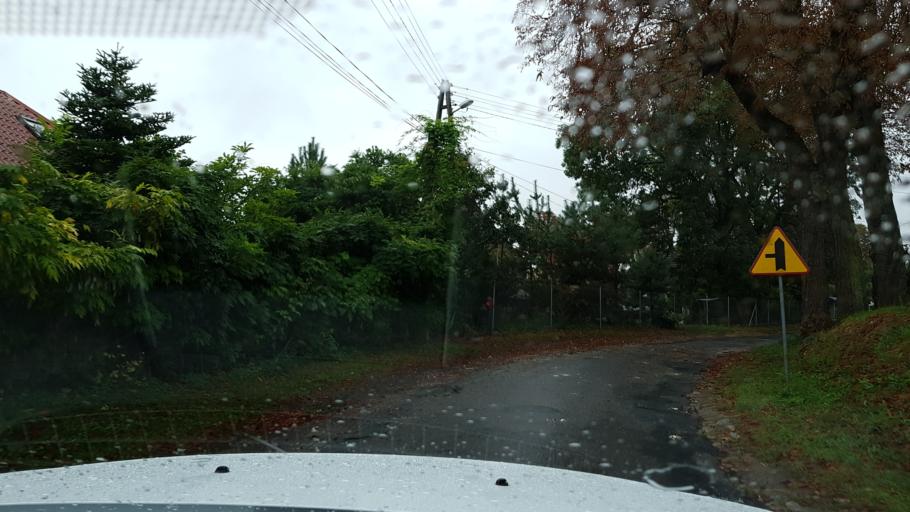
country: DE
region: Brandenburg
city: Schwedt (Oder)
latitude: 53.0184
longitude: 14.3150
